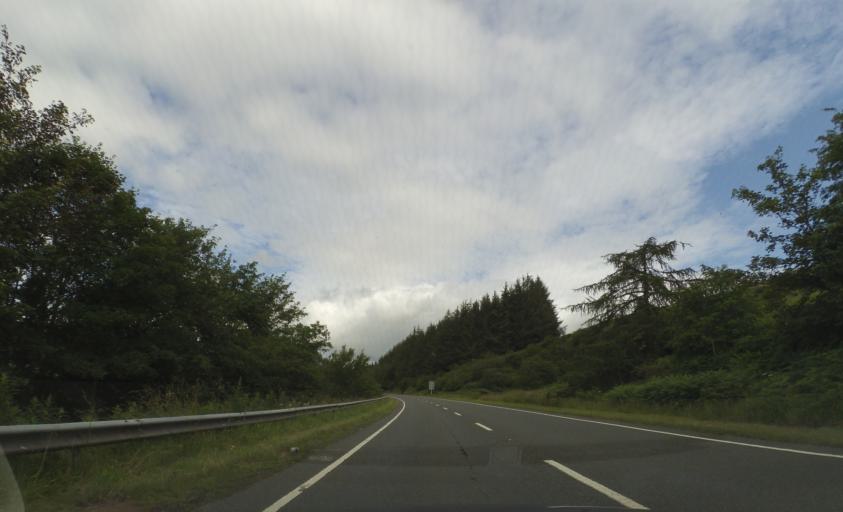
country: GB
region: Scotland
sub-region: The Scottish Borders
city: Selkirk
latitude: 55.5032
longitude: -2.8343
